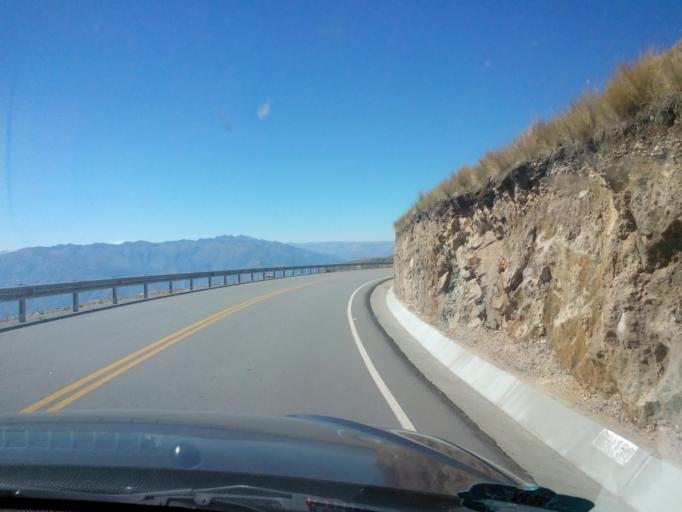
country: PE
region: Ayacucho
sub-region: Provincia de Huamanga
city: Ocros
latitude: -13.3921
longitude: -73.9538
